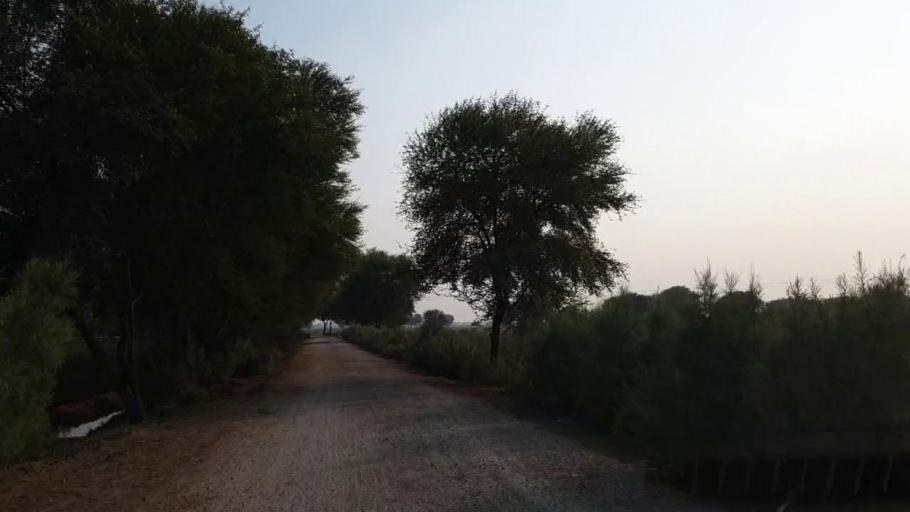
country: PK
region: Sindh
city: Bhan
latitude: 26.5007
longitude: 67.7633
